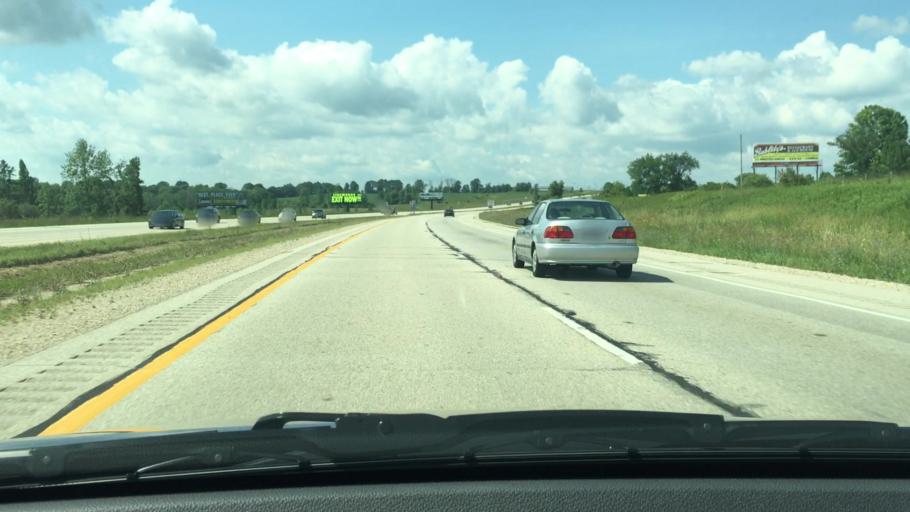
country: US
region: Wisconsin
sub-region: Dodge County
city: Theresa
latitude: 43.4583
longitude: -88.3649
